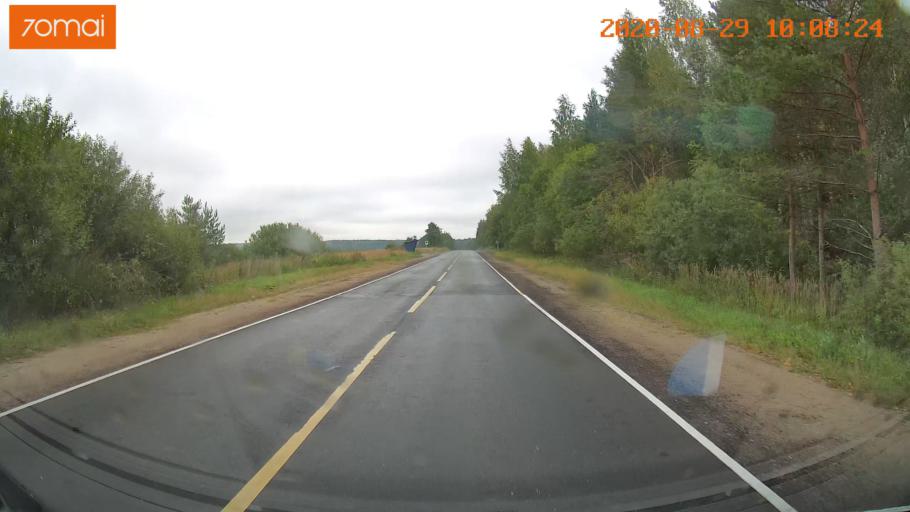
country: RU
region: Ivanovo
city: Kuznechikha
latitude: 57.3760
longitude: 42.5890
